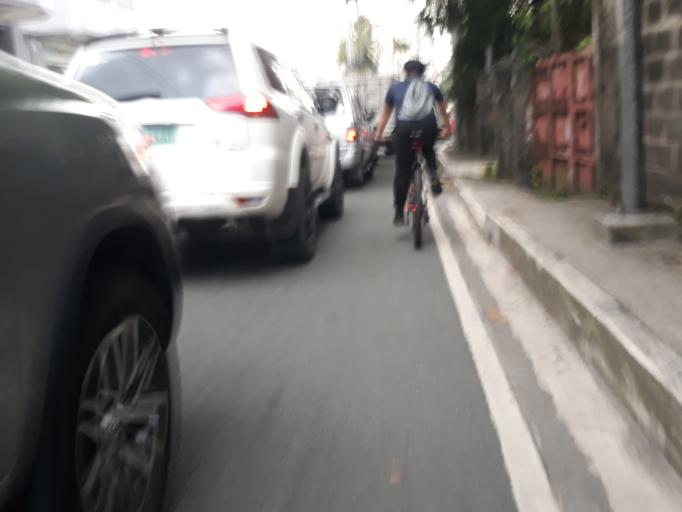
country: PH
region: Metro Manila
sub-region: San Juan
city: San Juan
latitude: 14.6013
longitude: 121.0358
